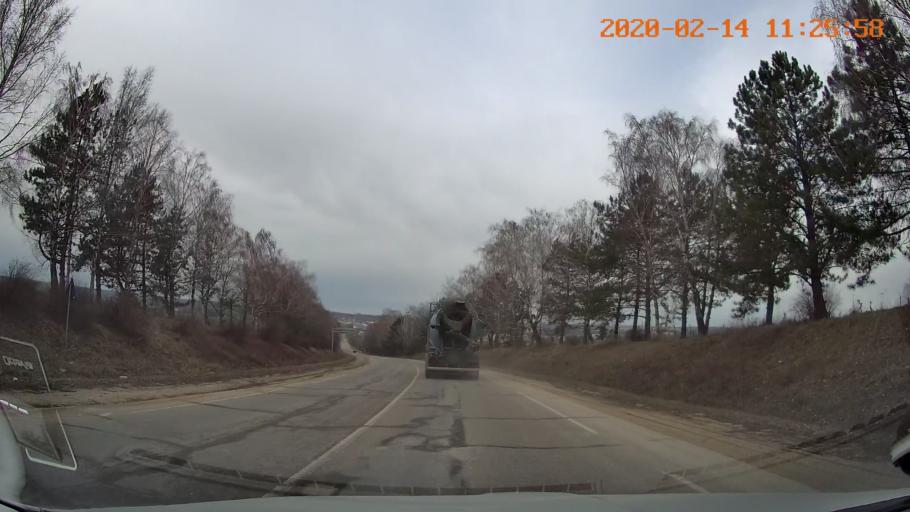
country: MD
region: Briceni
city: Briceni
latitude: 48.3522
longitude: 27.0979
